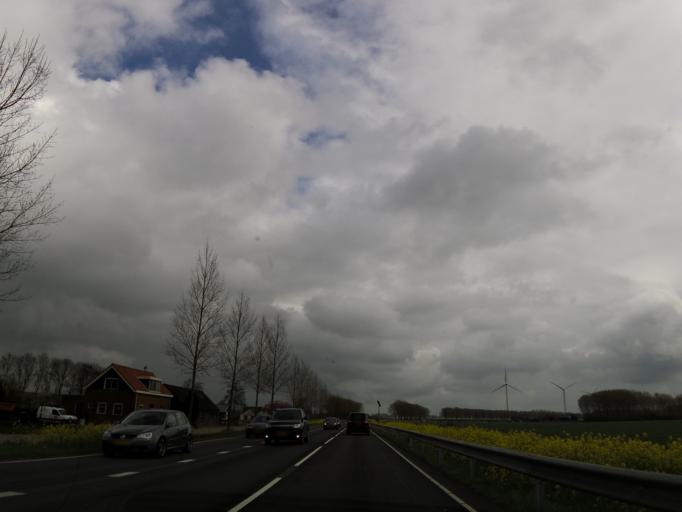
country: NL
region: Gelderland
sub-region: Gemeente Culemborg
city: Culemborg
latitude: 51.9328
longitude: 5.1762
